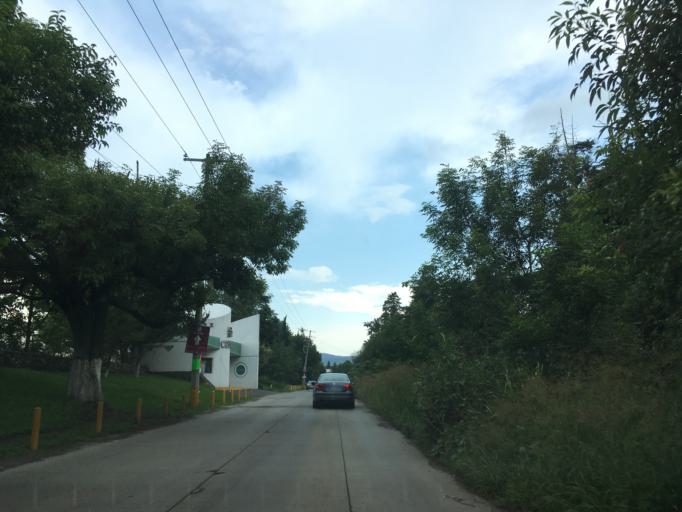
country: MX
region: Michoacan
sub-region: Morelia
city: Morelos
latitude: 19.6737
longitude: -101.2357
